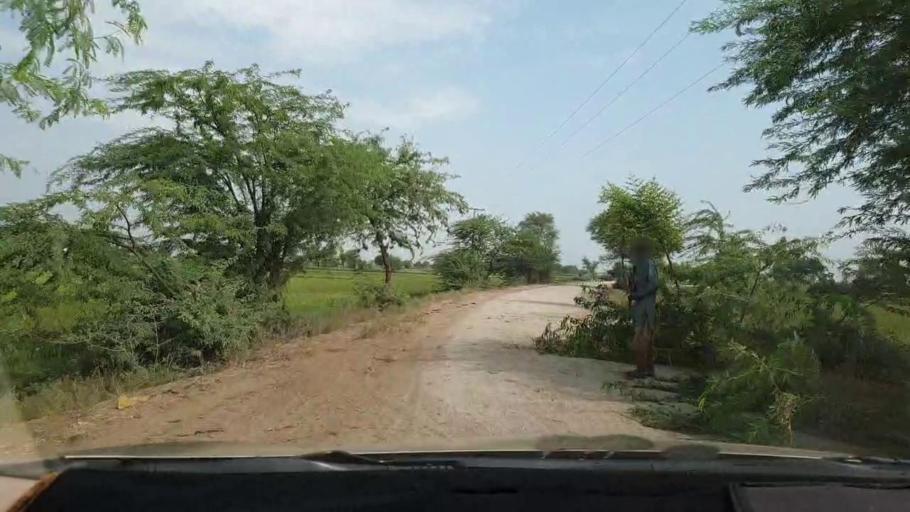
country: PK
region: Sindh
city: Larkana
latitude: 27.6741
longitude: 68.2203
